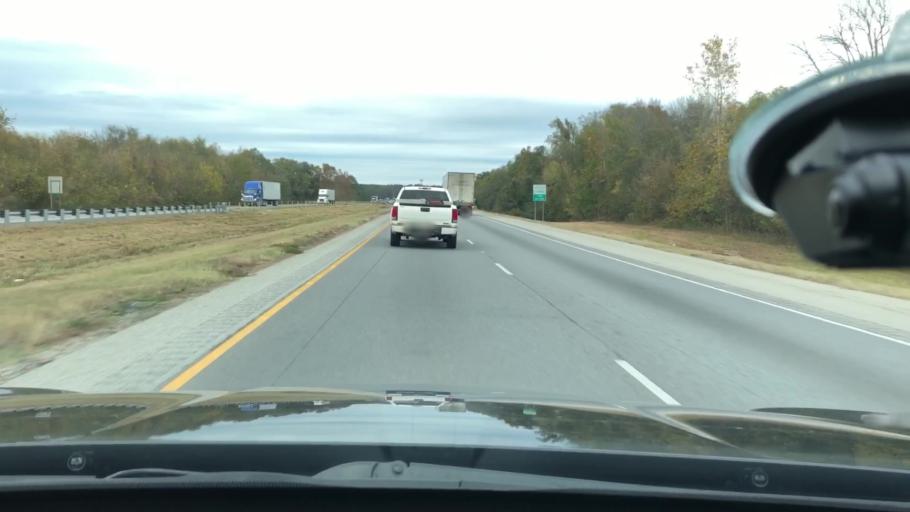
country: US
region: Arkansas
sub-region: Clark County
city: Arkadelphia
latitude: 34.1726
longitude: -93.0747
